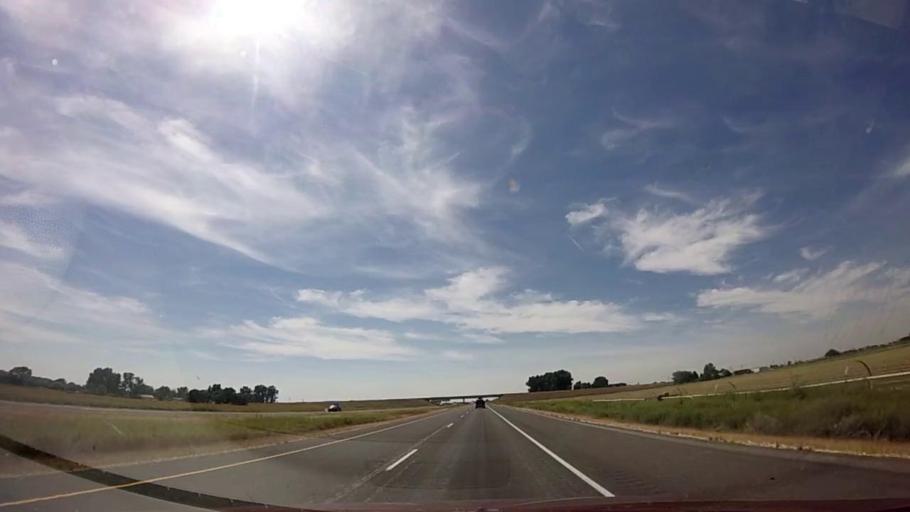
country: US
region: Idaho
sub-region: Minidoka County
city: Rupert
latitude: 42.5690
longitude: -113.7006
